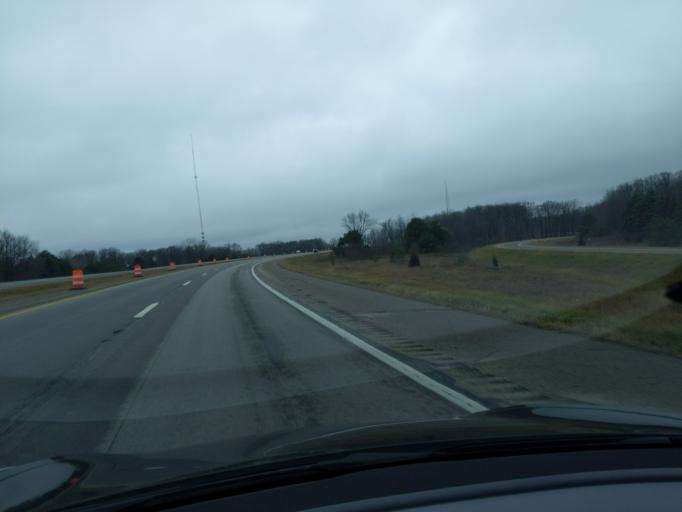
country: US
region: Michigan
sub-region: Ingham County
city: Holt
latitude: 42.6709
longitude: -84.4914
